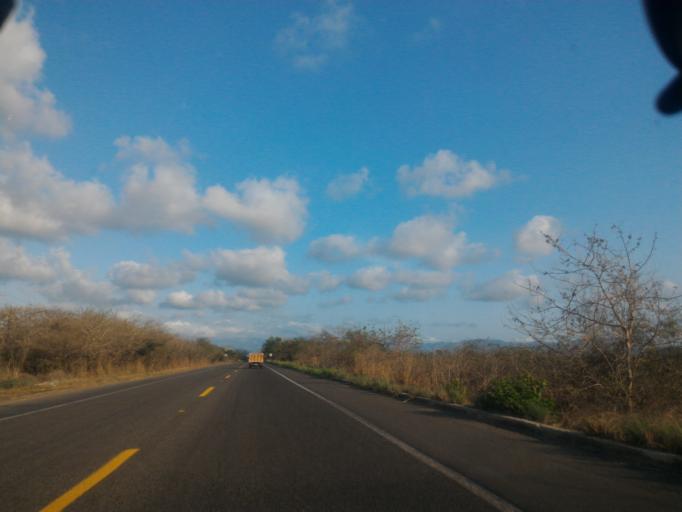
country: MX
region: Michoacan
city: Coahuayana Viejo
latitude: 18.7821
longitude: -103.7687
